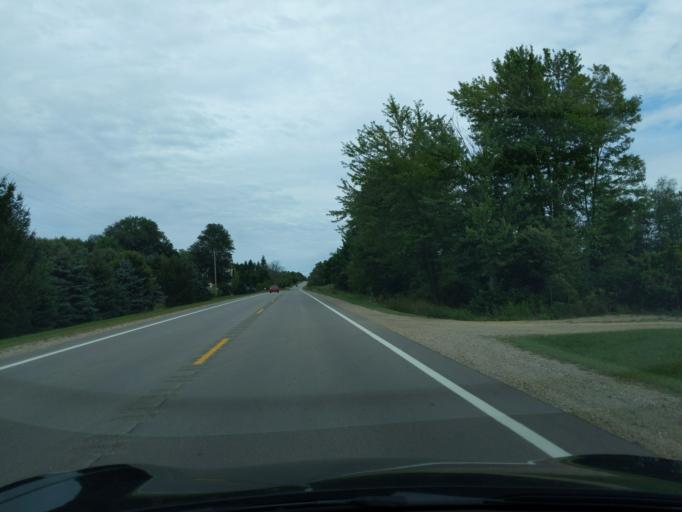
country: US
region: Michigan
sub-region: Barry County
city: Nashville
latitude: 42.5673
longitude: -85.0860
